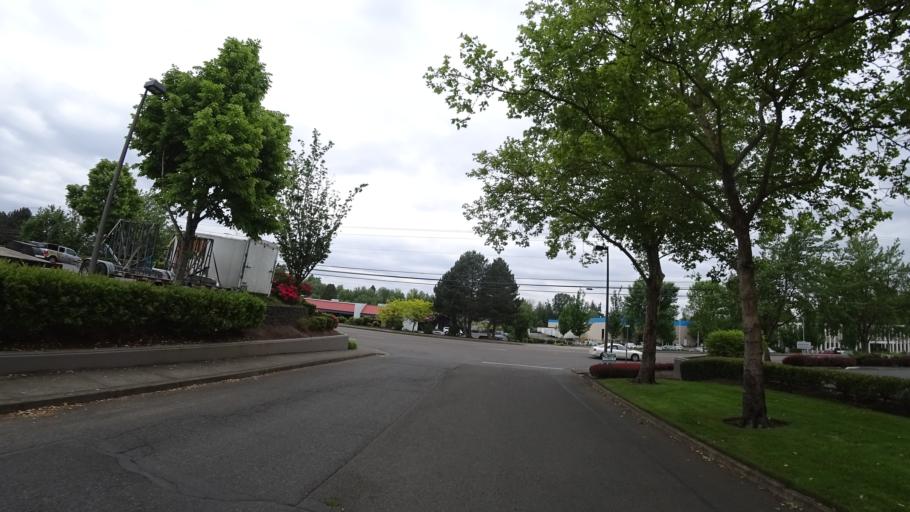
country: US
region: Oregon
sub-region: Washington County
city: Raleigh Hills
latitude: 45.4741
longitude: -122.7771
